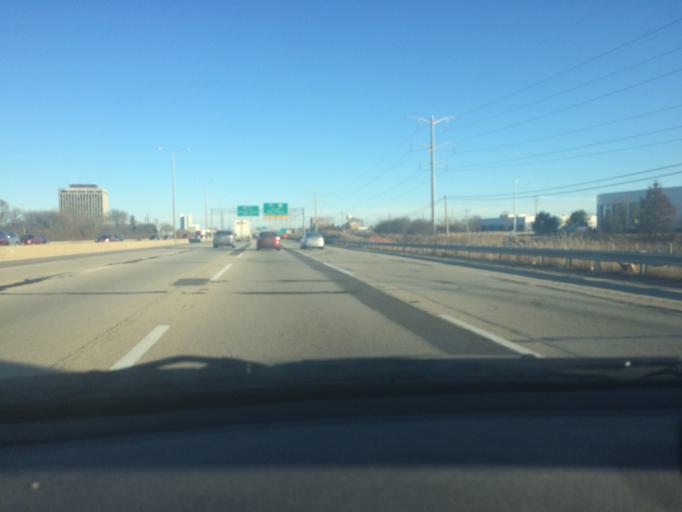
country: US
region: Illinois
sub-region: Cook County
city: Hoffman Estates
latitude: 42.0616
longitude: -88.0618
